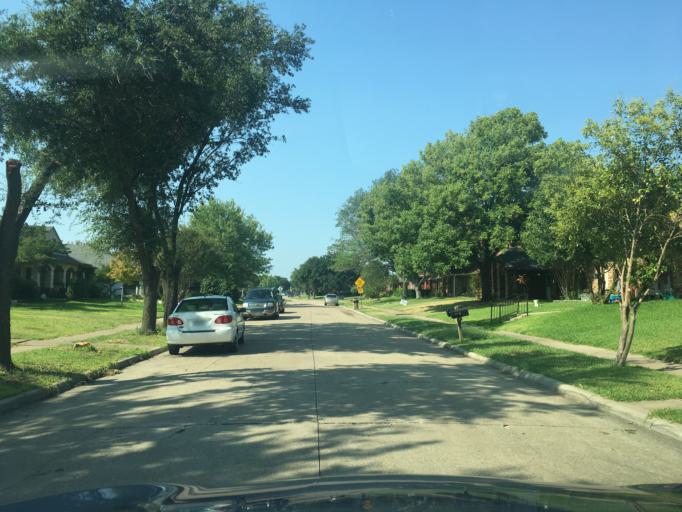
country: US
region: Texas
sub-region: Dallas County
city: Garland
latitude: 32.9430
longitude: -96.6309
